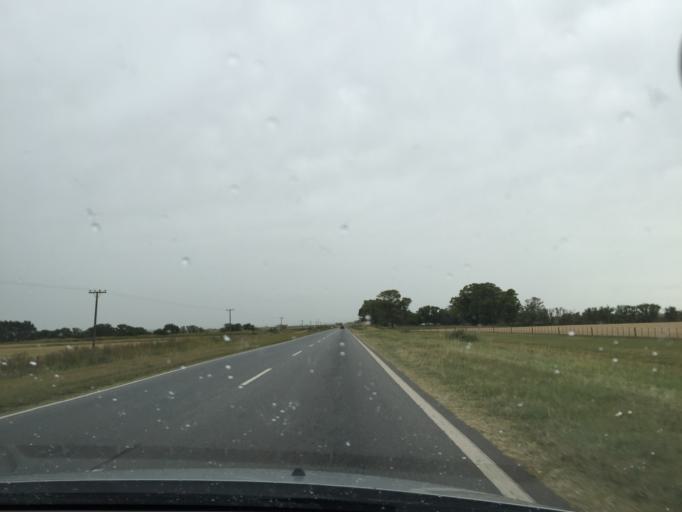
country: AR
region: Buenos Aires
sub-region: Partido de Tandil
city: Tandil
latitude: -37.5598
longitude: -58.7910
